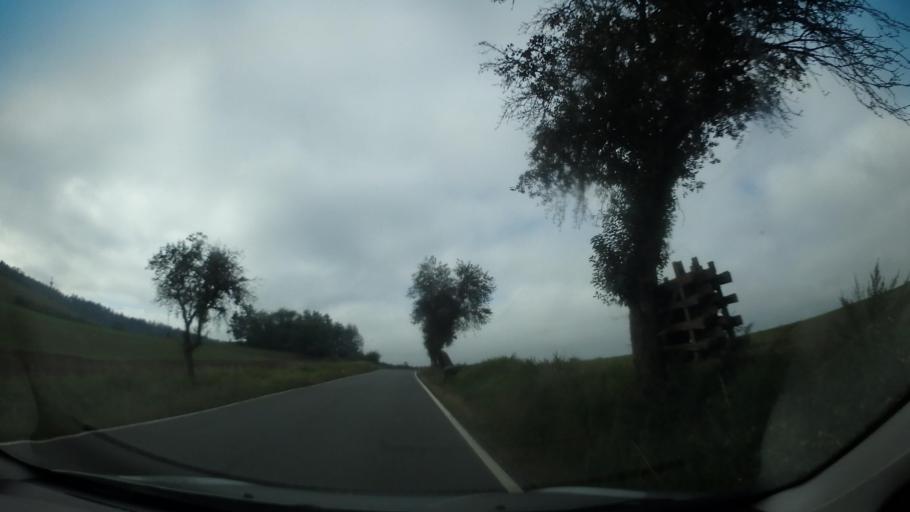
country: CZ
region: Central Bohemia
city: Sedlcany
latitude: 49.7074
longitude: 14.4526
